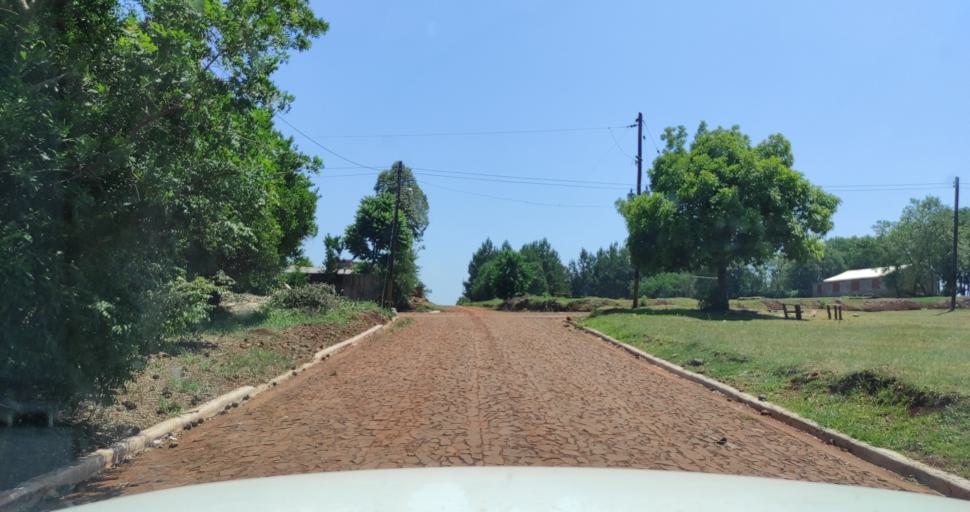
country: AR
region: Misiones
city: Santo Pipo
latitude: -27.1091
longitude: -55.3444
